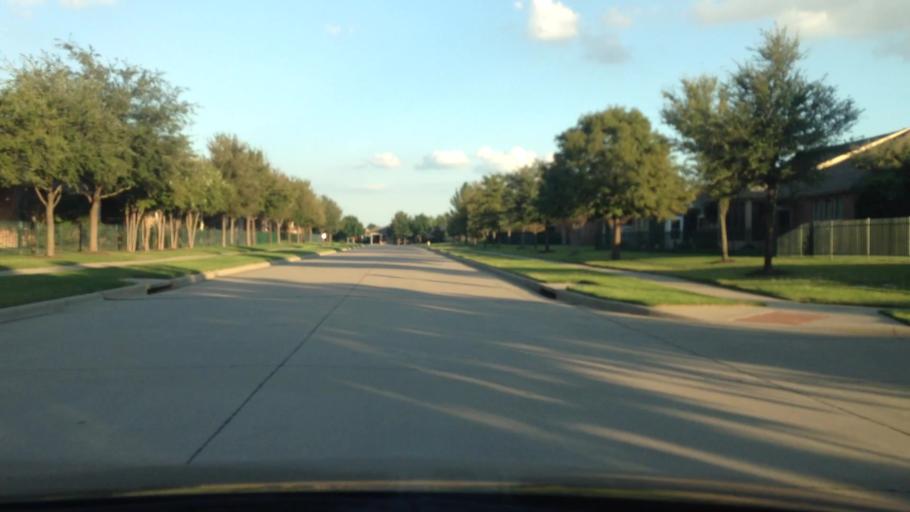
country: US
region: Texas
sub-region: Denton County
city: Little Elm
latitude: 33.1447
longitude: -96.9003
